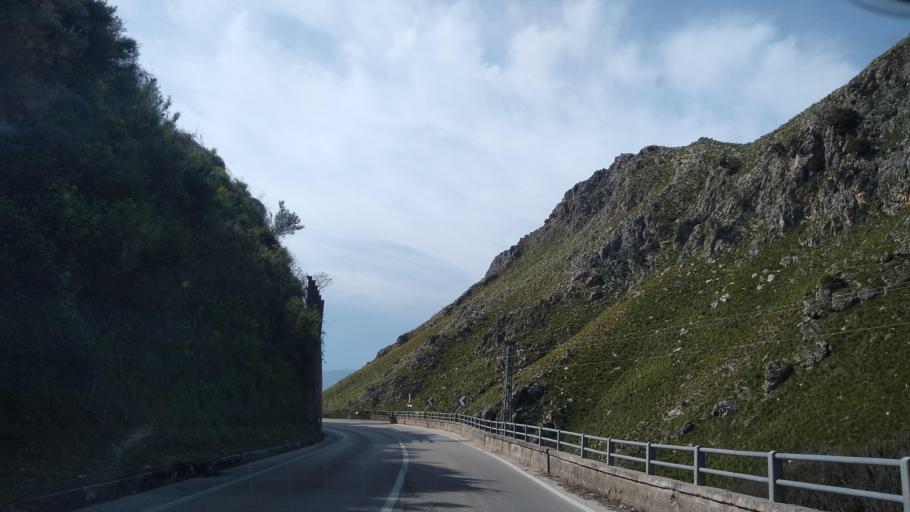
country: IT
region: Sicily
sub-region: Palermo
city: Pioppo
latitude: 38.0497
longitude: 13.1925
